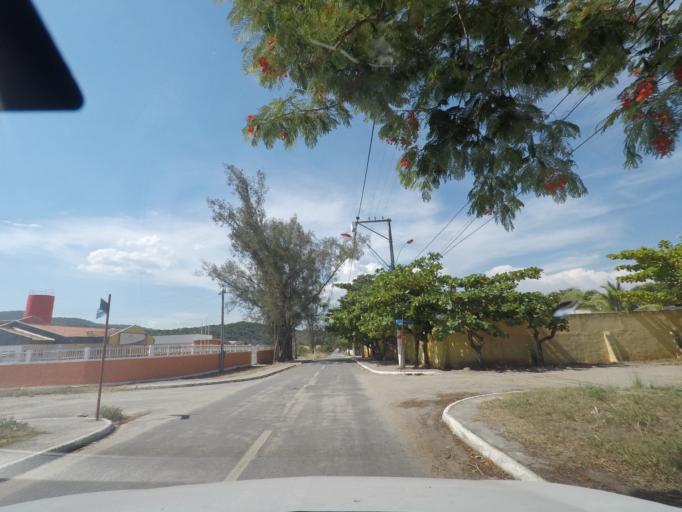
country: BR
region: Rio de Janeiro
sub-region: Marica
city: Marica
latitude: -22.9642
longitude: -42.9685
